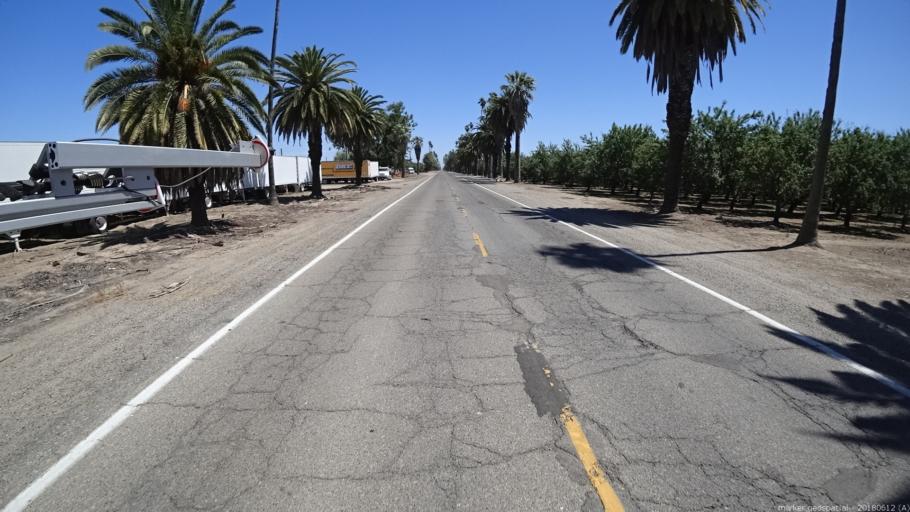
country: US
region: California
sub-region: Madera County
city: Chowchilla
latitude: 37.0599
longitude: -120.3176
